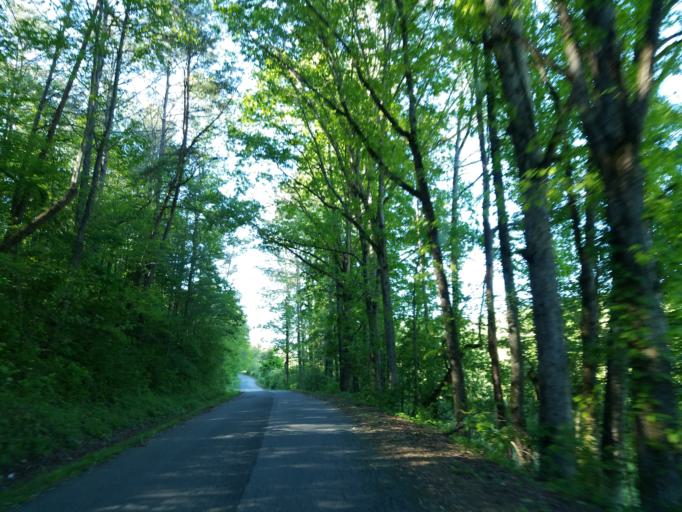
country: US
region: Georgia
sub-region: Gilmer County
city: Ellijay
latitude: 34.5822
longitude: -84.5098
